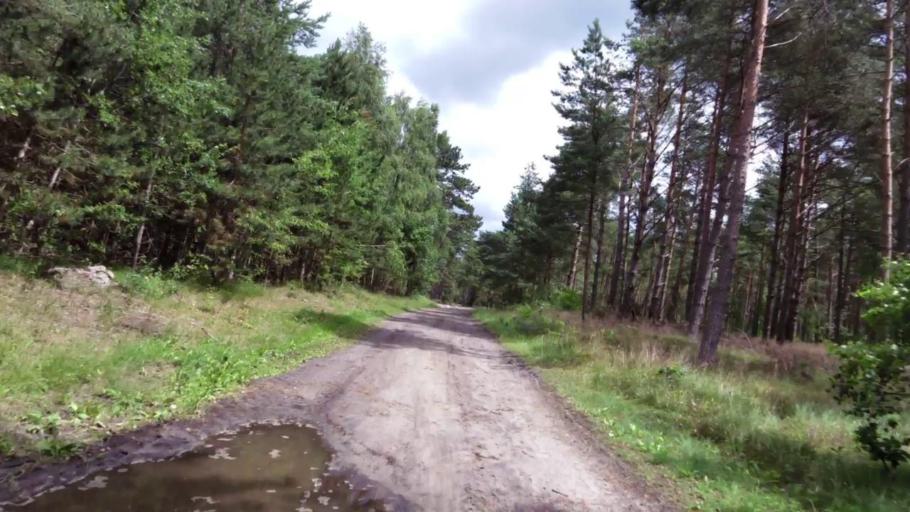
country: PL
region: West Pomeranian Voivodeship
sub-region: Powiat slawienski
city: Darlowo
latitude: 54.4996
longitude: 16.4537
